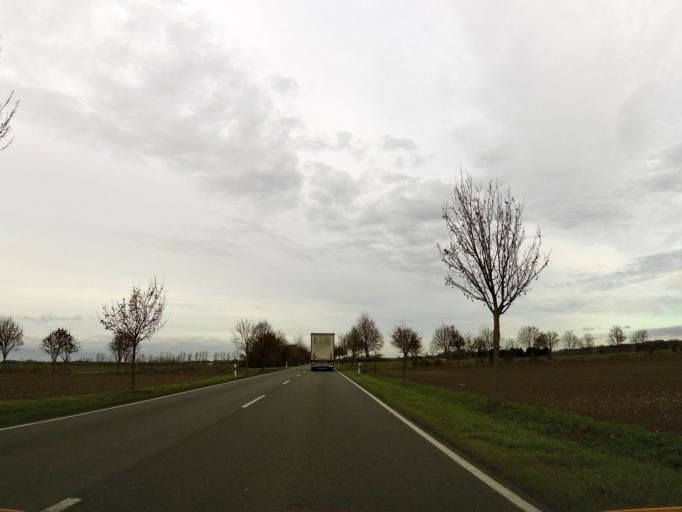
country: DE
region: Saxony-Anhalt
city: Pretzier
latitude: 52.7817
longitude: 11.2335
